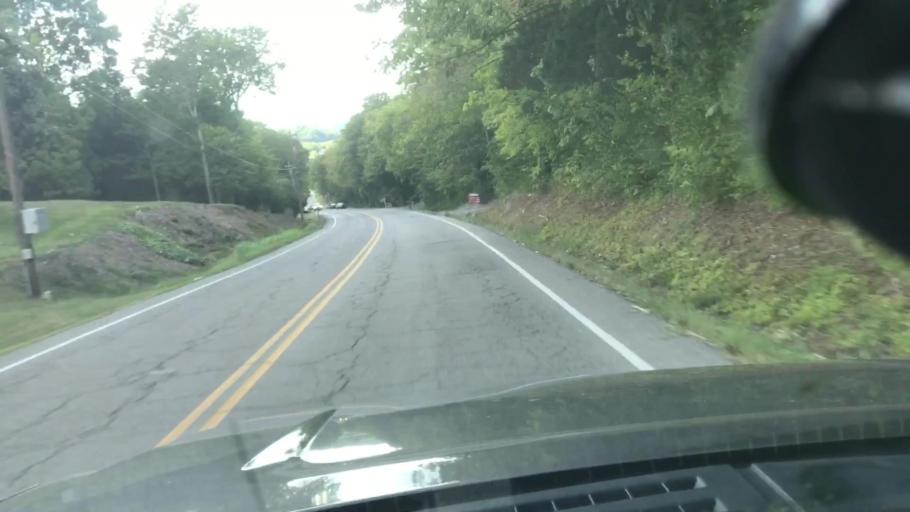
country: US
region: Tennessee
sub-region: Davidson County
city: Forest Hills
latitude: 36.0294
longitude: -86.9459
